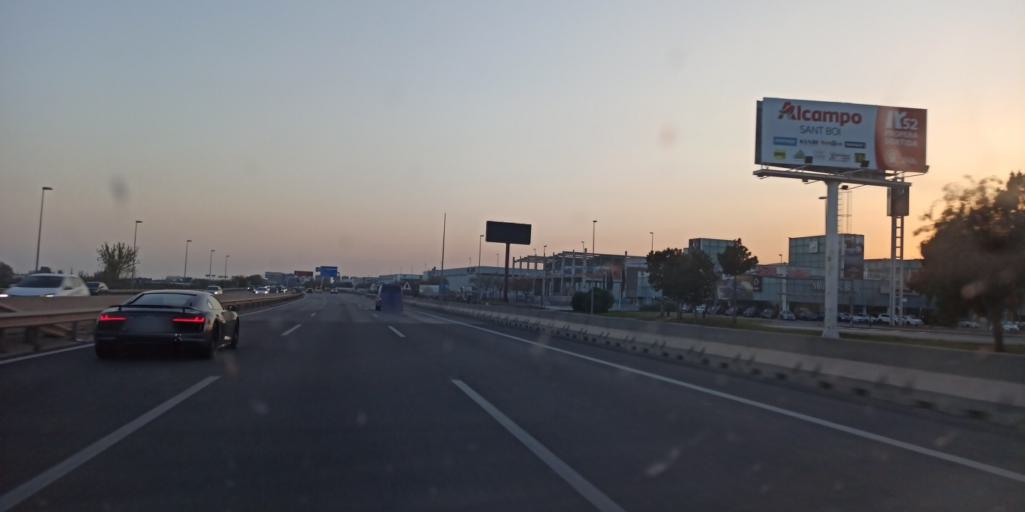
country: ES
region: Catalonia
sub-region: Provincia de Barcelona
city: Sant Boi de Llobregat
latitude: 41.3270
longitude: 2.0485
